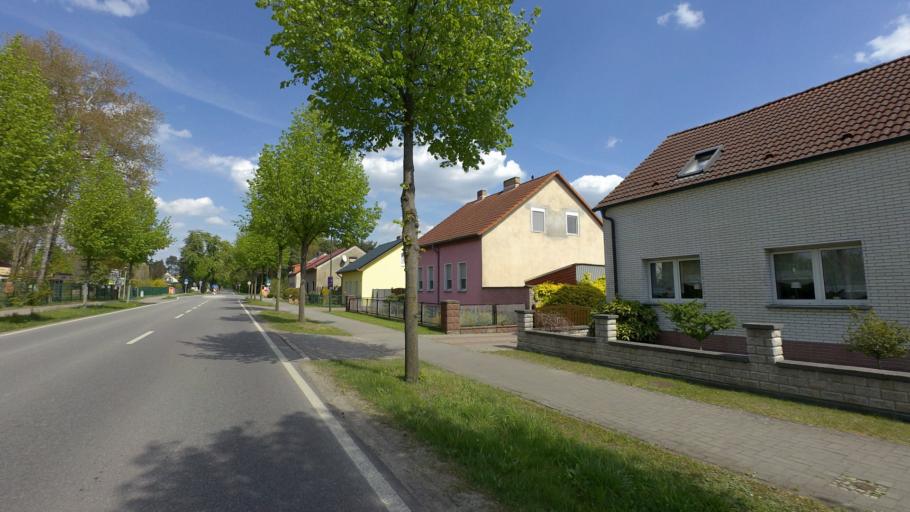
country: DE
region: Brandenburg
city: Wandlitz
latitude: 52.7998
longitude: 13.4825
